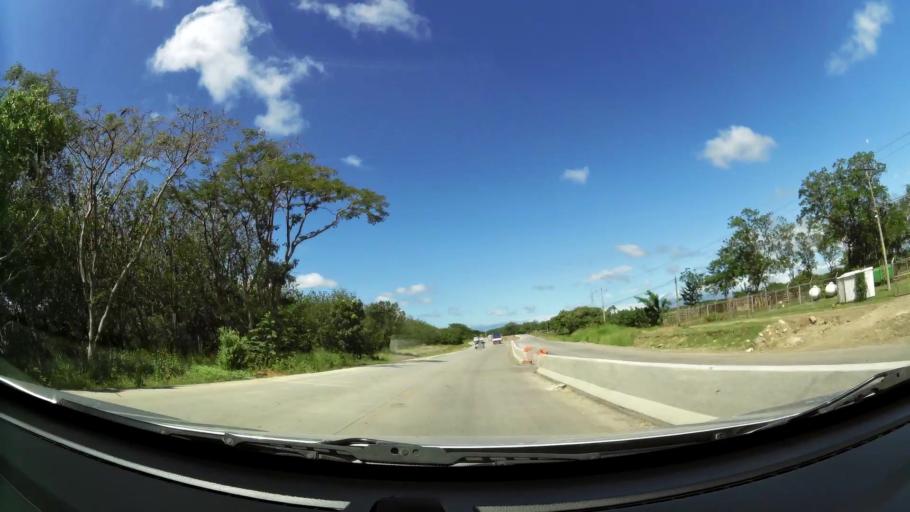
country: CR
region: Guanacaste
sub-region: Canton de Canas
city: Canas
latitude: 10.4347
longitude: -85.1051
